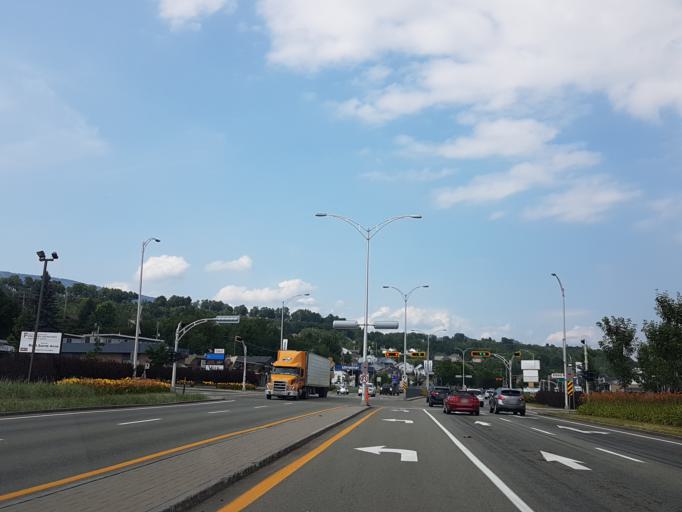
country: CA
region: Quebec
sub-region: Capitale-Nationale
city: Beaupre
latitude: 47.0408
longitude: -70.8971
